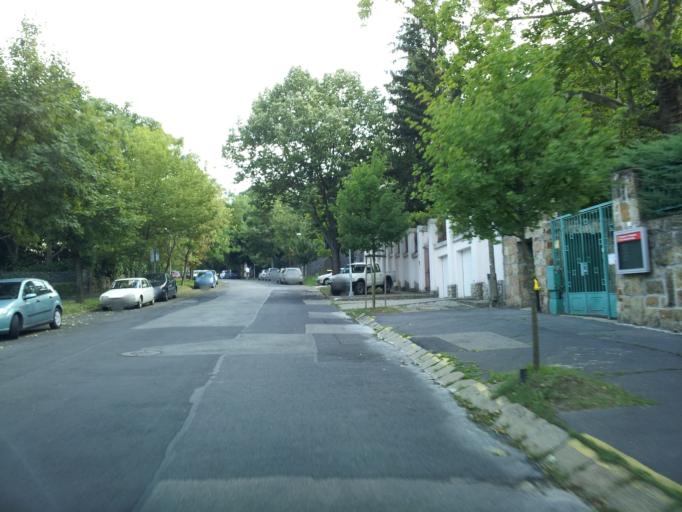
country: HU
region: Budapest
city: Budapest XII. keruelet
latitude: 47.5035
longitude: 19.0154
